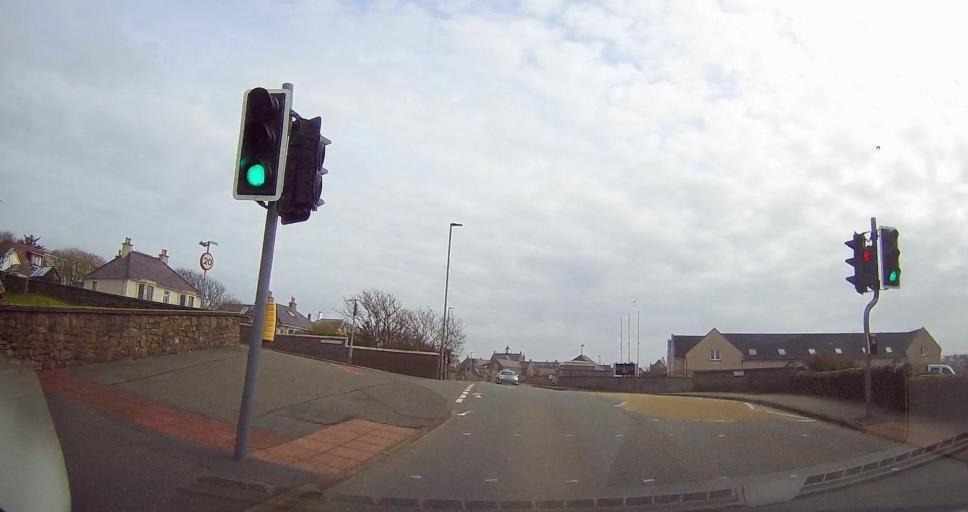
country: GB
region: Scotland
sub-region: Shetland Islands
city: Lerwick
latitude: 60.1507
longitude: -1.1545
